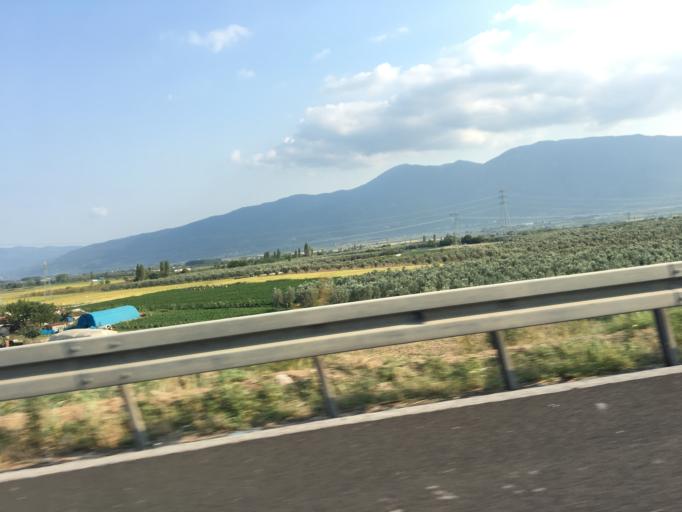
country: TR
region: Bursa
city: Orhangazi
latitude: 40.4619
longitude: 29.3024
